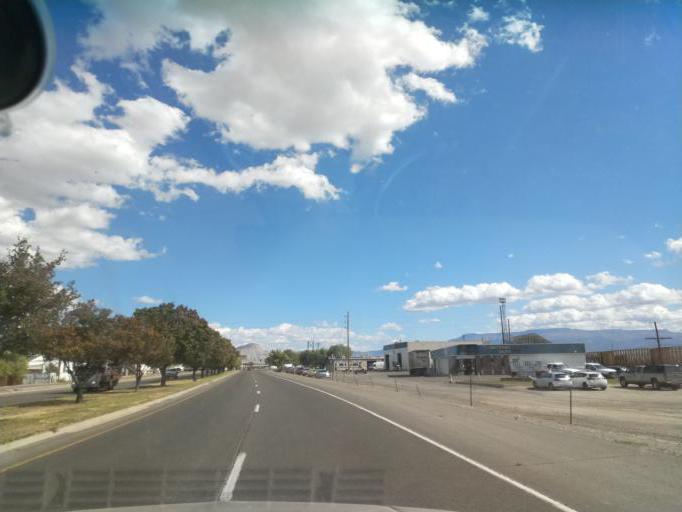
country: US
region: Colorado
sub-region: Mesa County
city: Grand Junction
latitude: 39.0654
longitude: -108.5462
